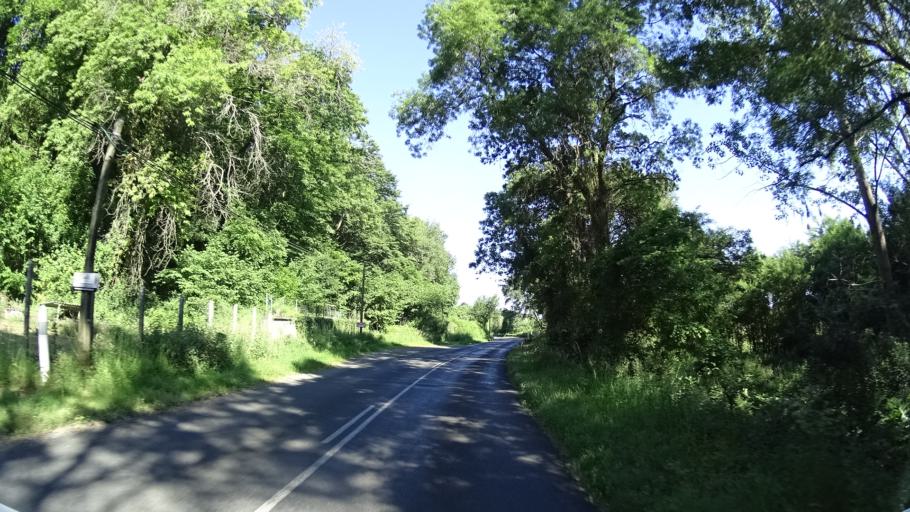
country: FR
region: Pays de la Loire
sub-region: Departement de Maine-et-Loire
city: Saint-Martin-de-la-Place
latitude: 47.2880
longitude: -0.1312
